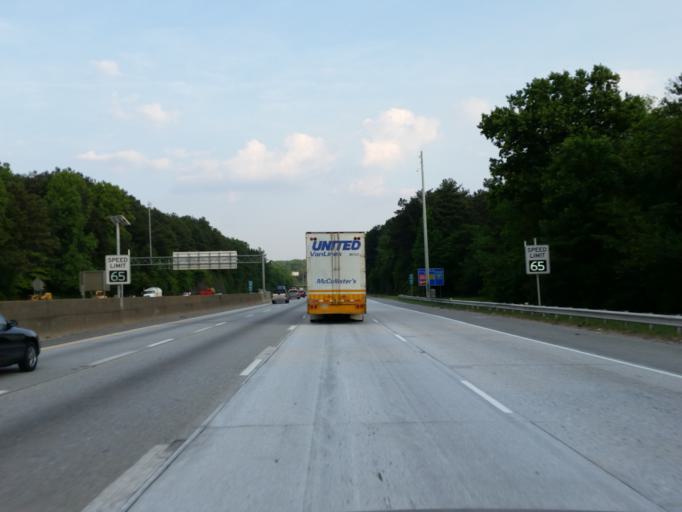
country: US
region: Georgia
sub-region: Cobb County
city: Vinings
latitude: 33.8055
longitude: -84.4929
